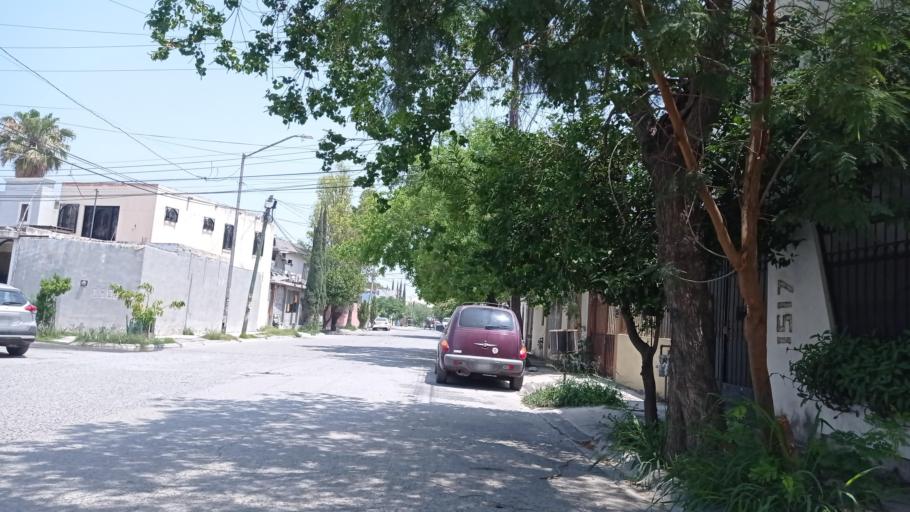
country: MX
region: Nuevo Leon
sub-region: Juarez
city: Jardines de la Silla (Jardines)
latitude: 25.6534
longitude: -100.1905
